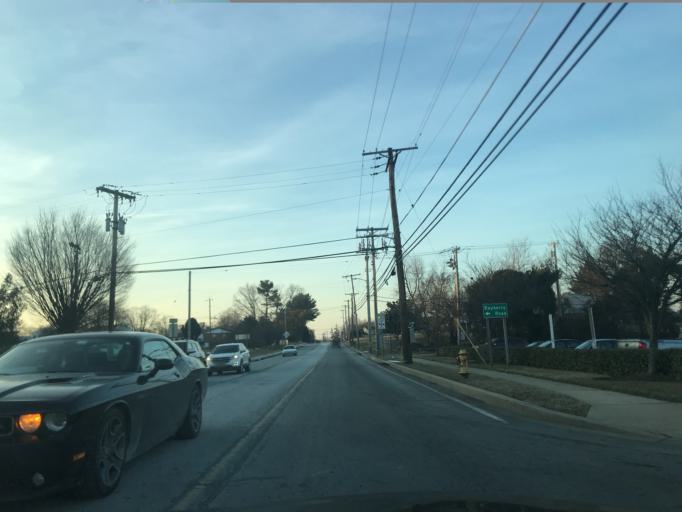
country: US
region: Maryland
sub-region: Harford County
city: Edgewood
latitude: 39.4270
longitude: -76.2996
